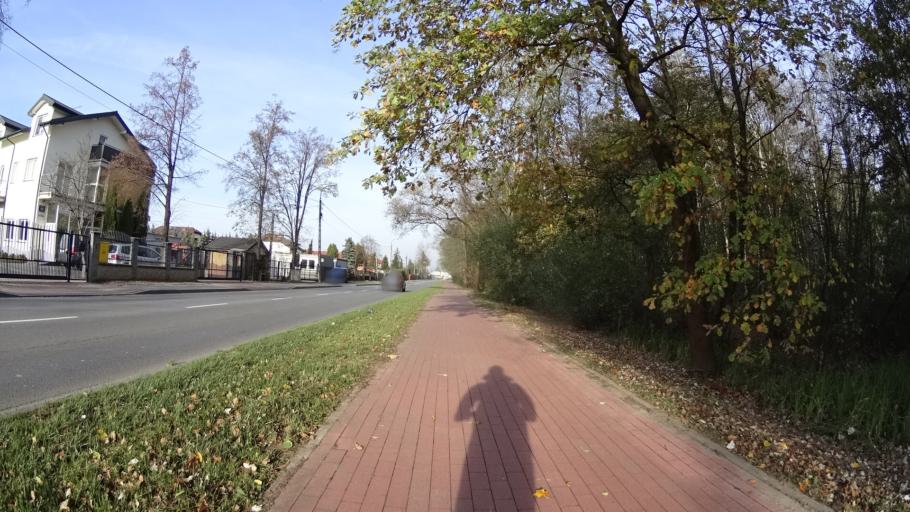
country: PL
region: Masovian Voivodeship
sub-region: Powiat warszawski zachodni
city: Babice
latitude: 52.2722
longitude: 20.8632
